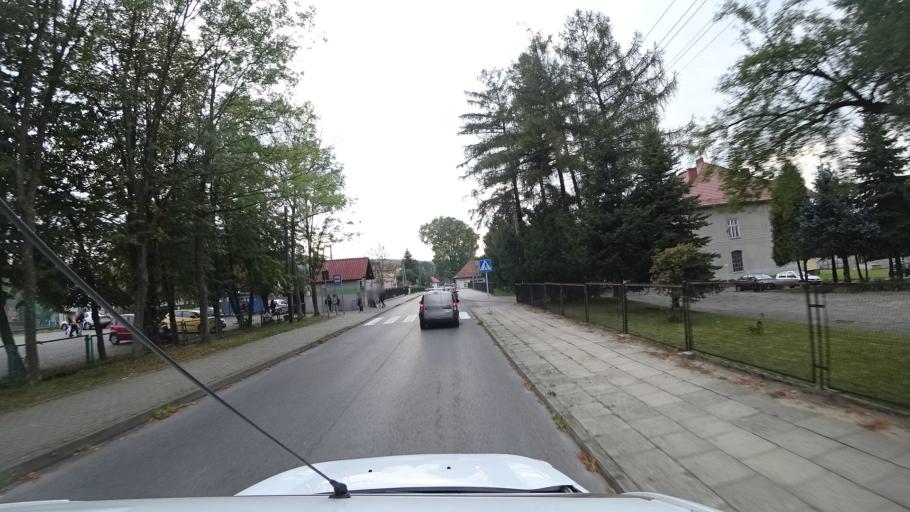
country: PL
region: Lesser Poland Voivodeship
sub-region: Powiat wadowicki
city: Kalwaria Zebrzydowska
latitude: 49.8682
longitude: 19.6801
